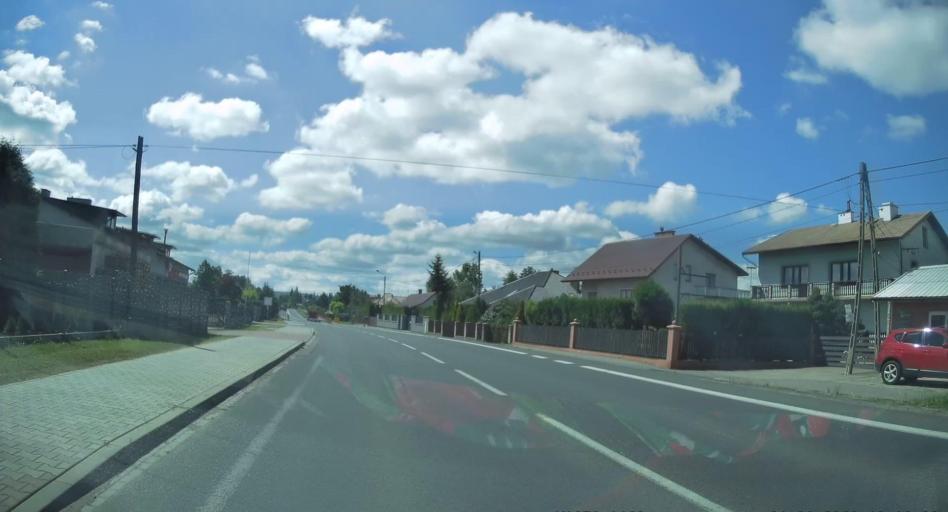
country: PL
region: Subcarpathian Voivodeship
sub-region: Powiat debicki
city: Brzeznica
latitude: 50.0758
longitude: 21.4512
